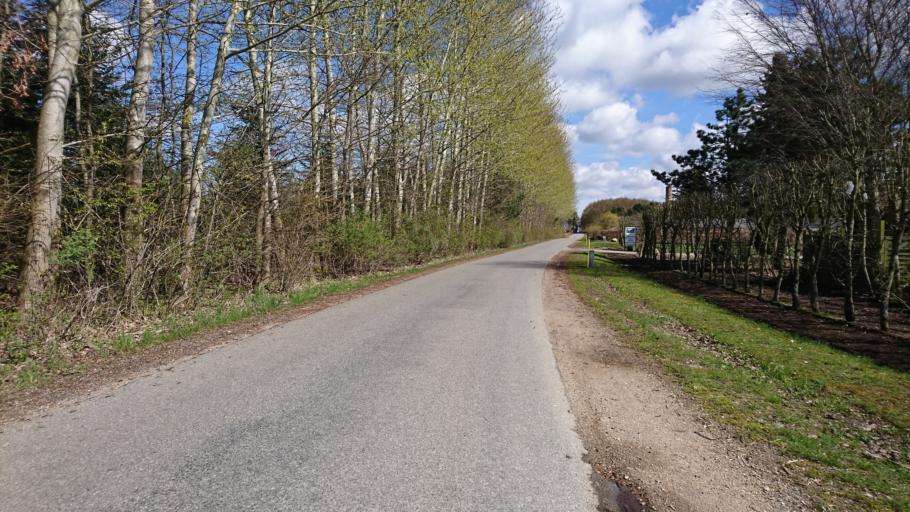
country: DK
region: Capital Region
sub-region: Egedal Kommune
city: Vekso
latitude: 55.7673
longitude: 12.2473
